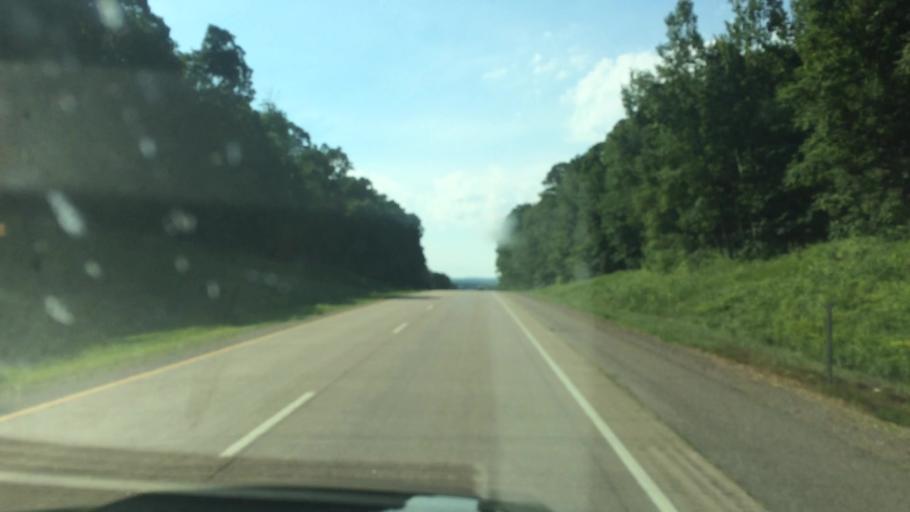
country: US
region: Wisconsin
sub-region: Shawano County
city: Wittenberg
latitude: 44.8215
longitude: -89.0571
